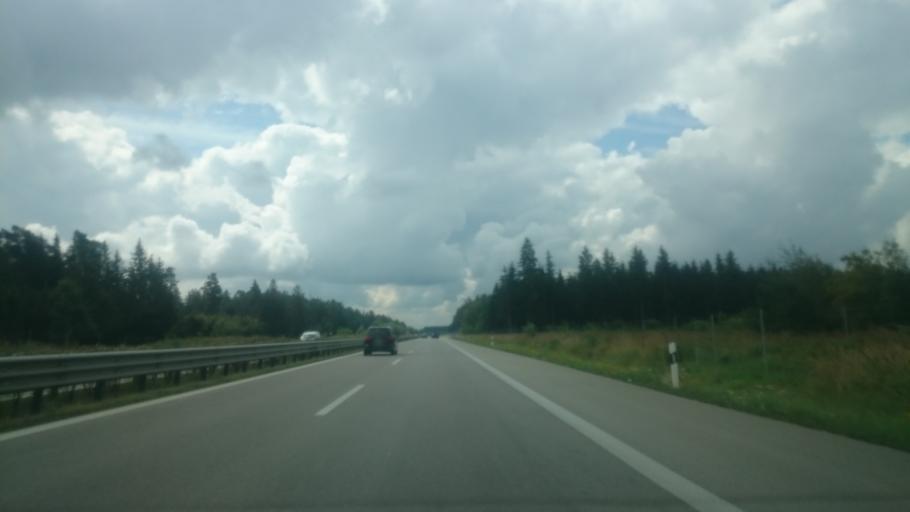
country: DE
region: Bavaria
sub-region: Upper Bavaria
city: Hurlach
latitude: 48.1024
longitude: 10.8366
